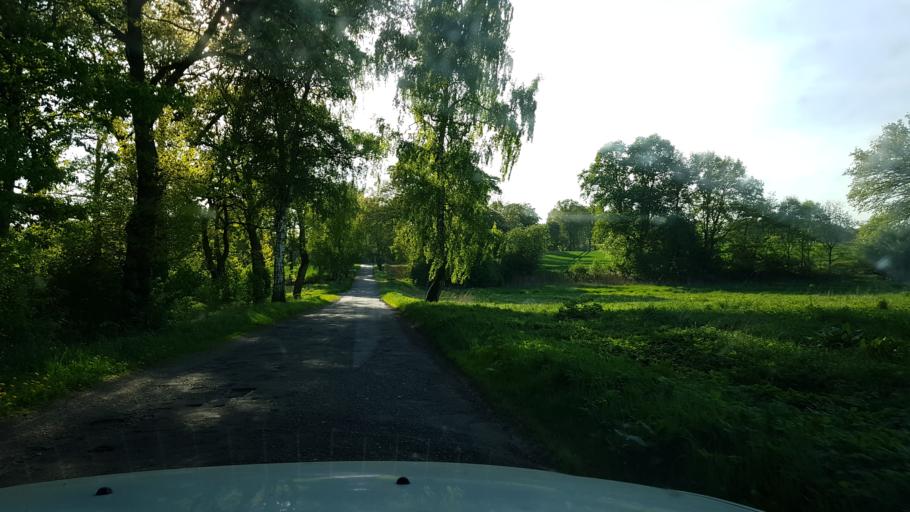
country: PL
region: West Pomeranian Voivodeship
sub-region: Powiat lobeski
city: Dobra
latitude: 53.6353
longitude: 15.3698
